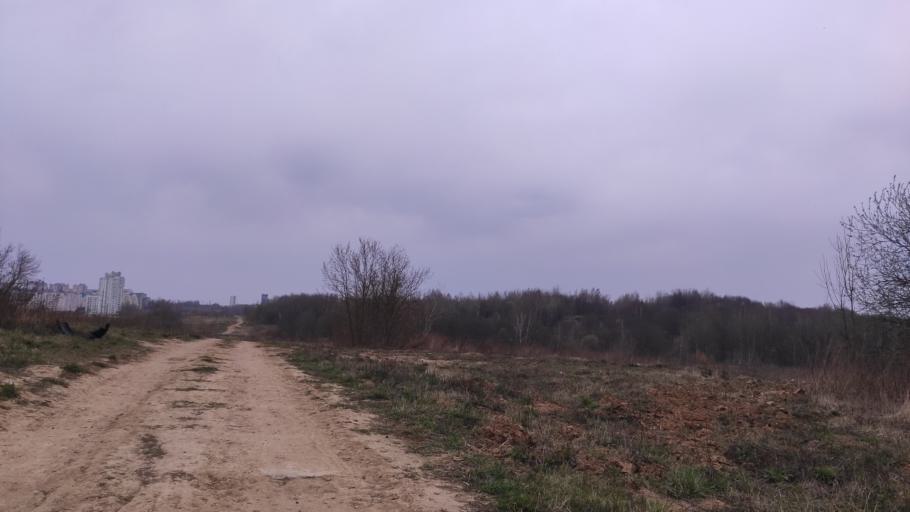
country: BY
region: Minsk
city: Novoye Medvezhino
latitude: 53.8845
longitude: 27.4644
